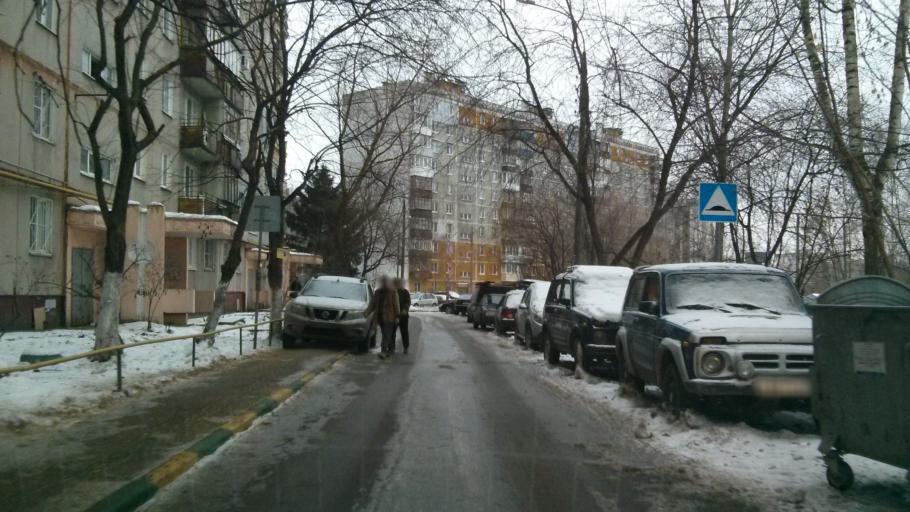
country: RU
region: Nizjnij Novgorod
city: Afonino
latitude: 56.2968
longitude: 44.0762
